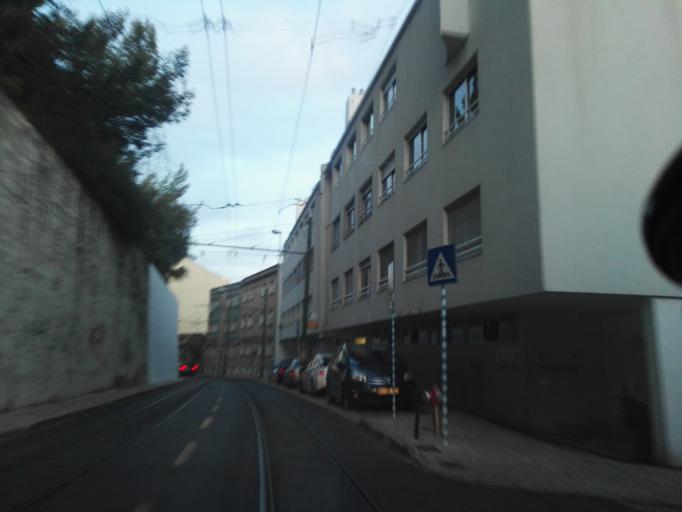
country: PT
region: Lisbon
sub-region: Oeiras
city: Linda-a-Velha
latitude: 38.7003
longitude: -9.2468
